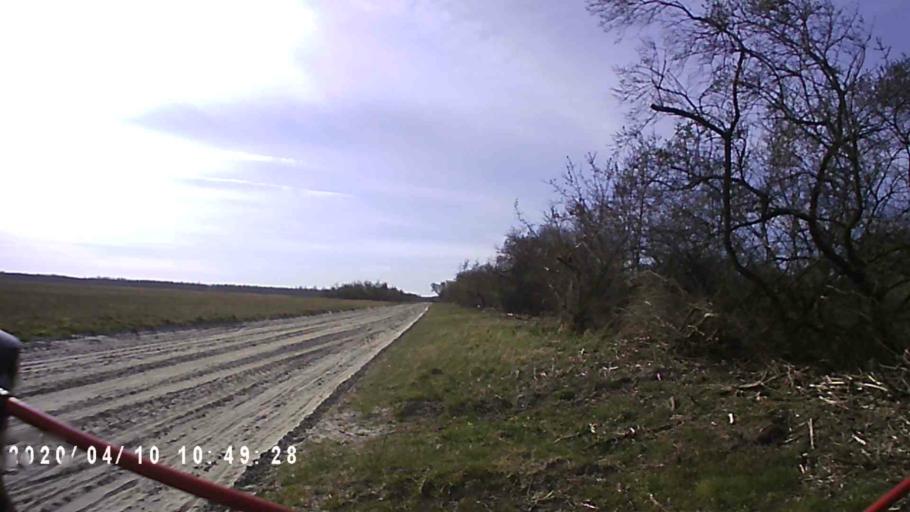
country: NL
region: Groningen
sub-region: Gemeente De Marne
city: Ulrum
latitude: 53.3835
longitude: 6.2402
